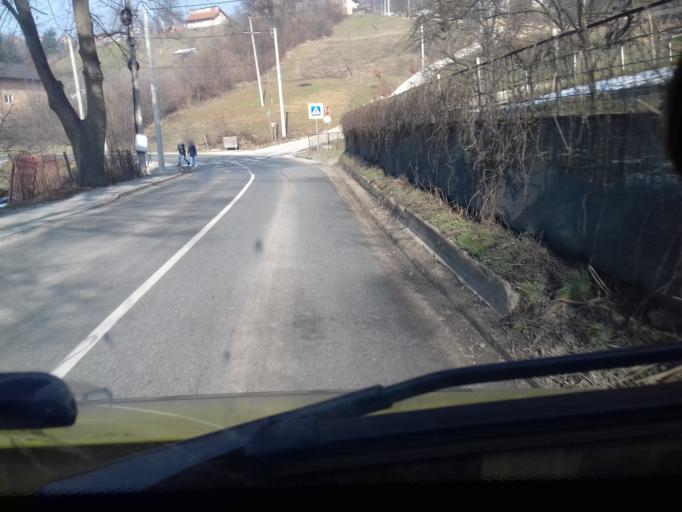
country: BA
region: Federation of Bosnia and Herzegovina
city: Vogosca
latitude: 43.9252
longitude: 18.3096
